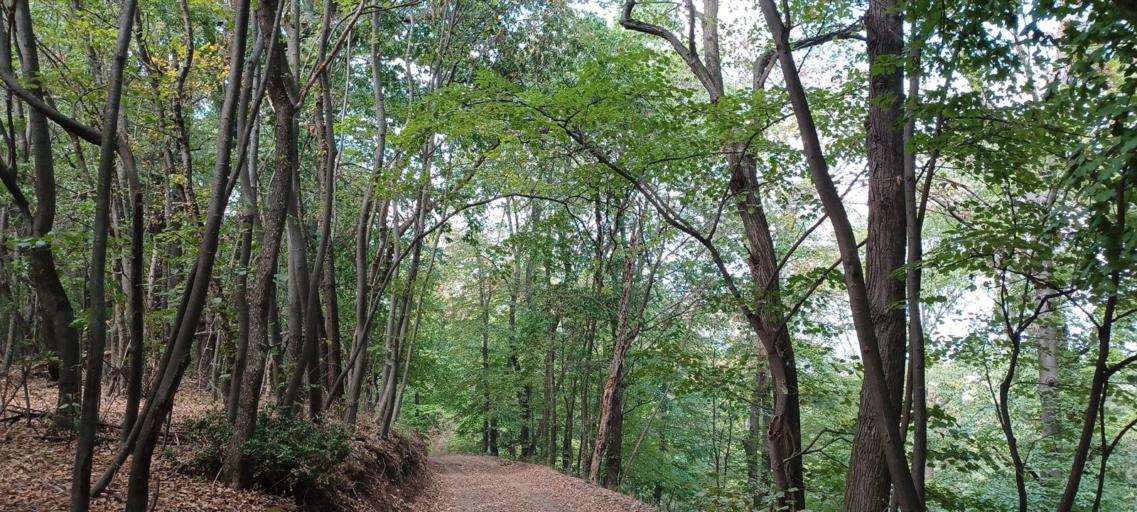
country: HU
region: Tolna
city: Szentgalpuszta
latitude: 46.3222
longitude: 18.6261
